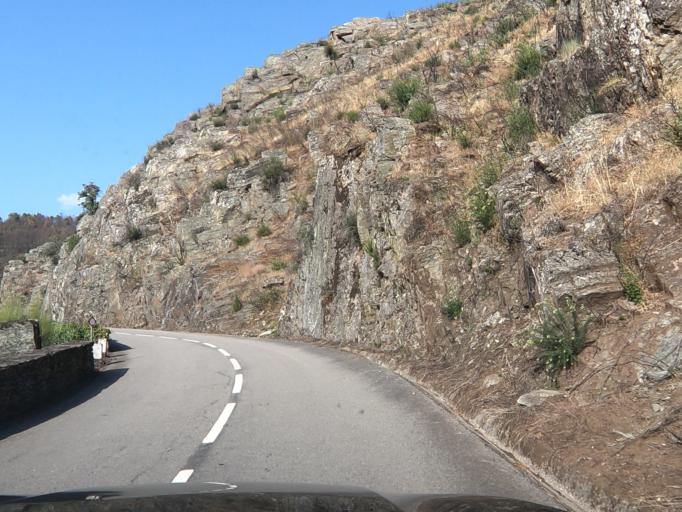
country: PT
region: Vila Real
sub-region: Sabrosa
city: Vilela
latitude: 41.2121
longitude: -7.6162
